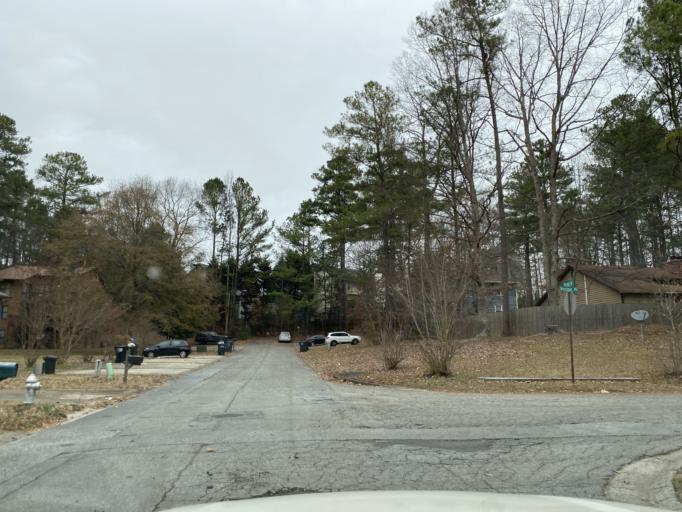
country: US
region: Georgia
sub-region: Cobb County
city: Fair Oaks
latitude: 33.9137
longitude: -84.5788
